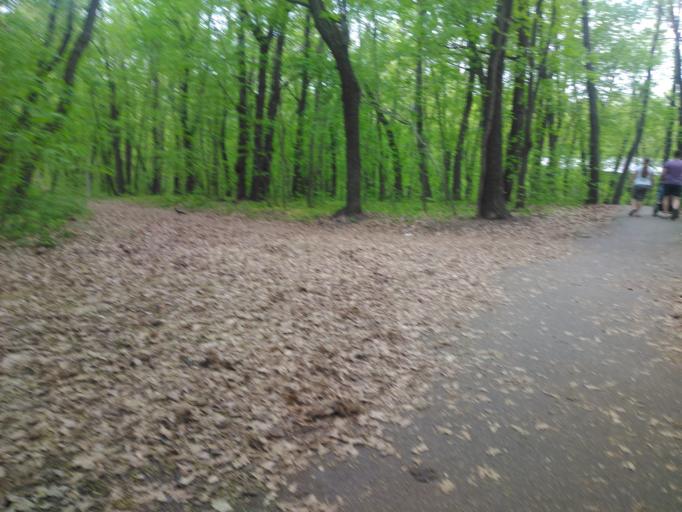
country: RU
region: Ulyanovsk
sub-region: Ulyanovskiy Rayon
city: Ulyanovsk
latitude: 54.2739
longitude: 48.3400
